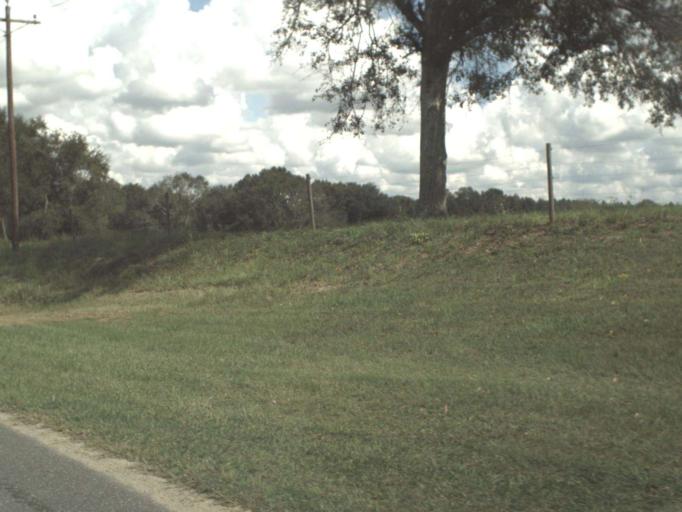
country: US
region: Florida
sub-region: Washington County
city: Chipley
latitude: 30.8096
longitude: -85.5117
